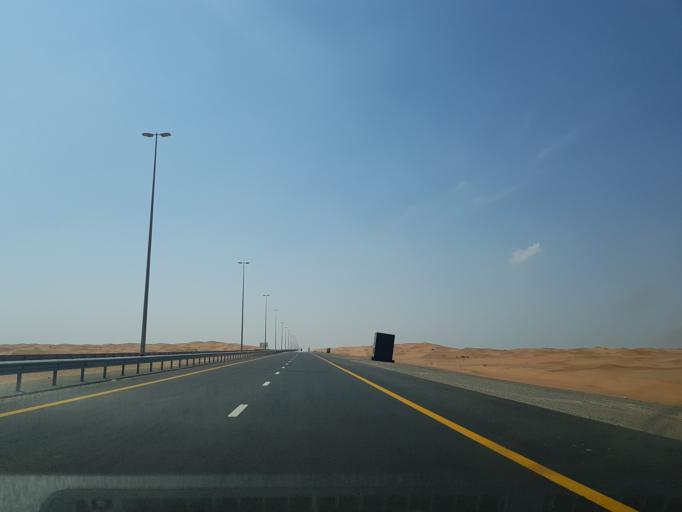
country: AE
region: Ash Shariqah
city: Adh Dhayd
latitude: 25.2515
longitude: 55.7854
